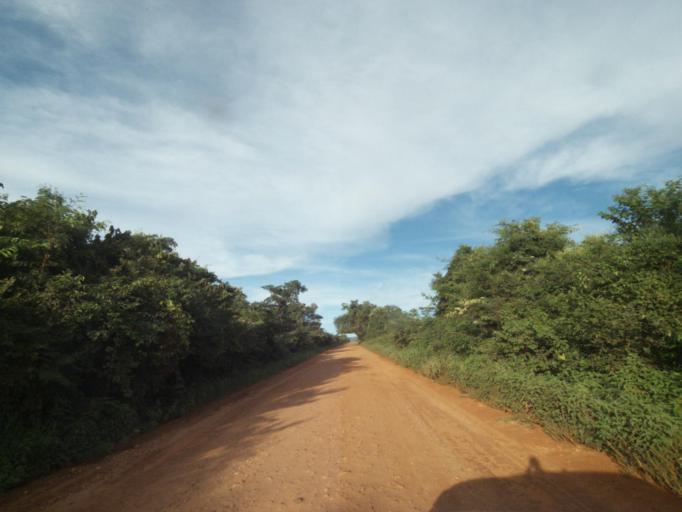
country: BR
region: Goias
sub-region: Jaragua
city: Jaragua
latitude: -15.8541
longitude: -49.3817
